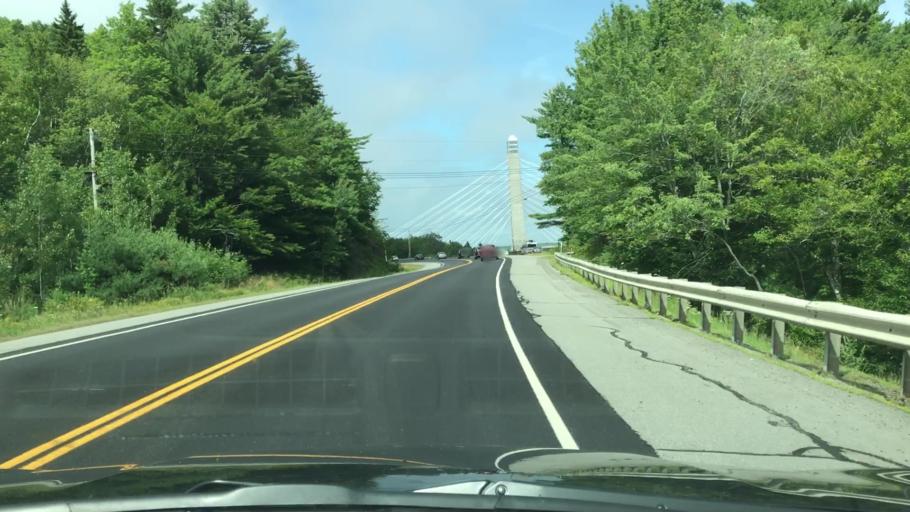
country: US
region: Maine
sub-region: Hancock County
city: Bucksport
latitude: 44.5559
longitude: -68.8091
